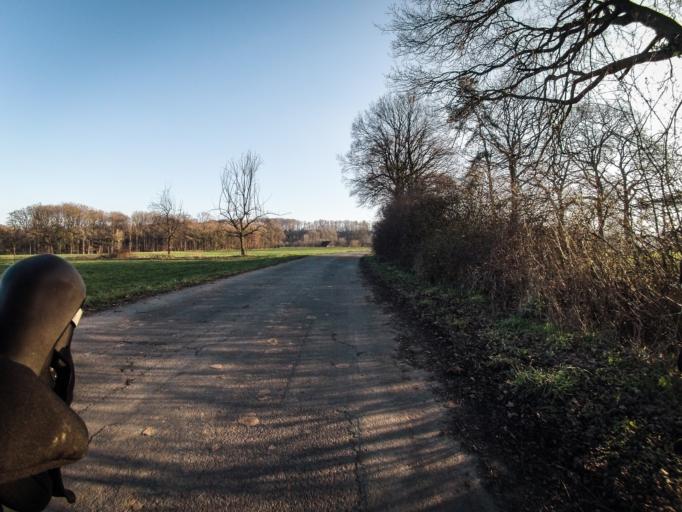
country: DE
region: North Rhine-Westphalia
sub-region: Regierungsbezirk Munster
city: Tecklenburg
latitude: 52.2522
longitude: 7.8331
